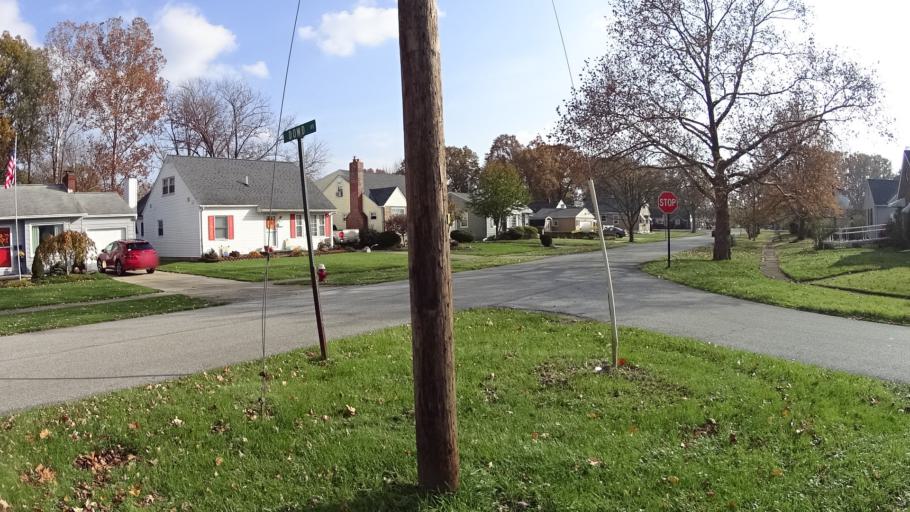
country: US
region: Ohio
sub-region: Lorain County
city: Elyria
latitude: 41.3887
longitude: -82.0892
